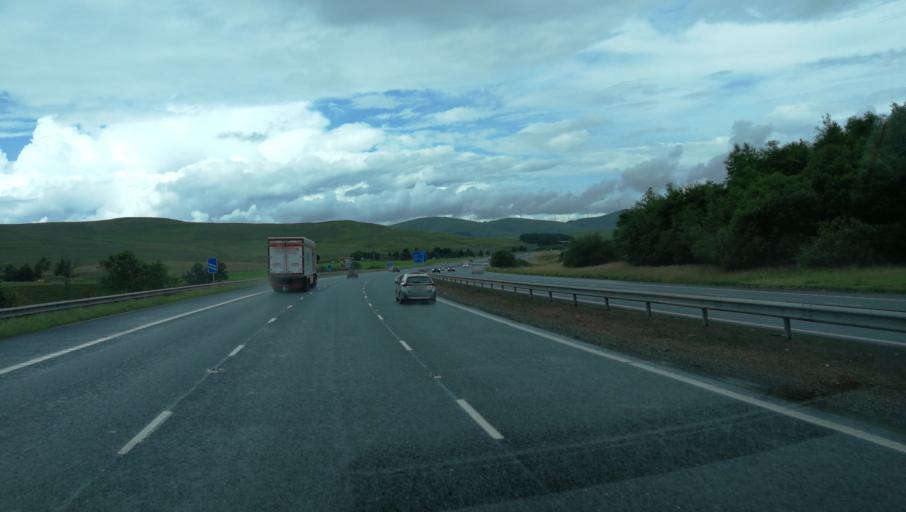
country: GB
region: Scotland
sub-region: South Lanarkshire
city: Biggar
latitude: 55.4437
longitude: -3.6525
